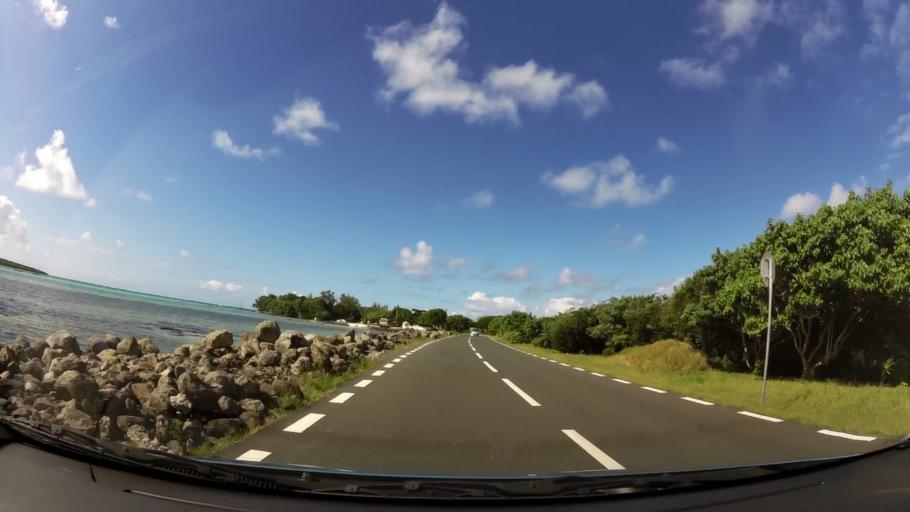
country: MU
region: Grand Port
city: Mahebourg
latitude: -20.4239
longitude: 57.7223
